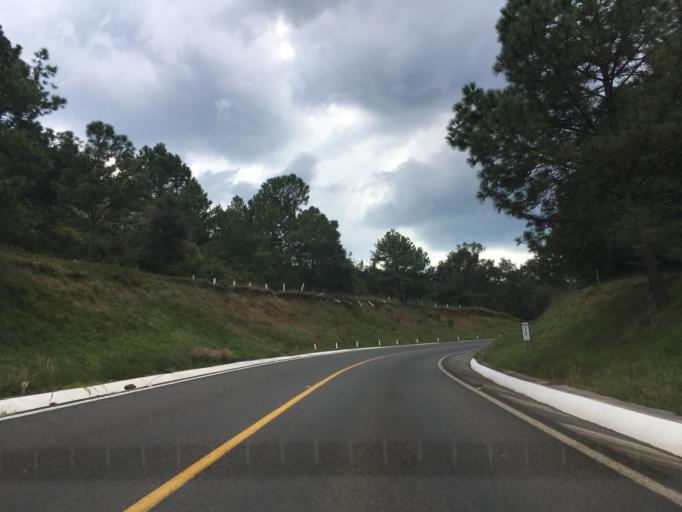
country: MX
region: Michoacan
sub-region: Patzcuaro
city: Santa Ana Chapitiro
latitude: 19.5045
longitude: -101.7022
